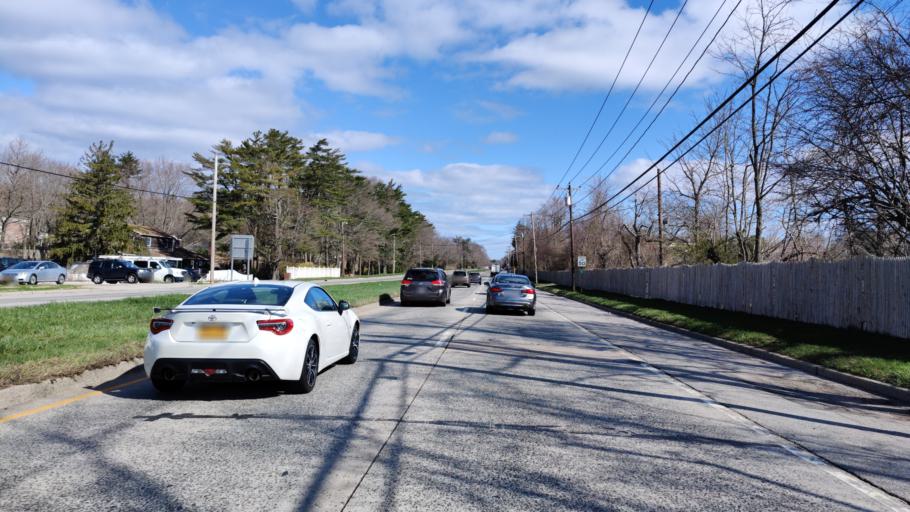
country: US
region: New York
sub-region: Suffolk County
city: Dix Hills
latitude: 40.8047
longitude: -73.3424
